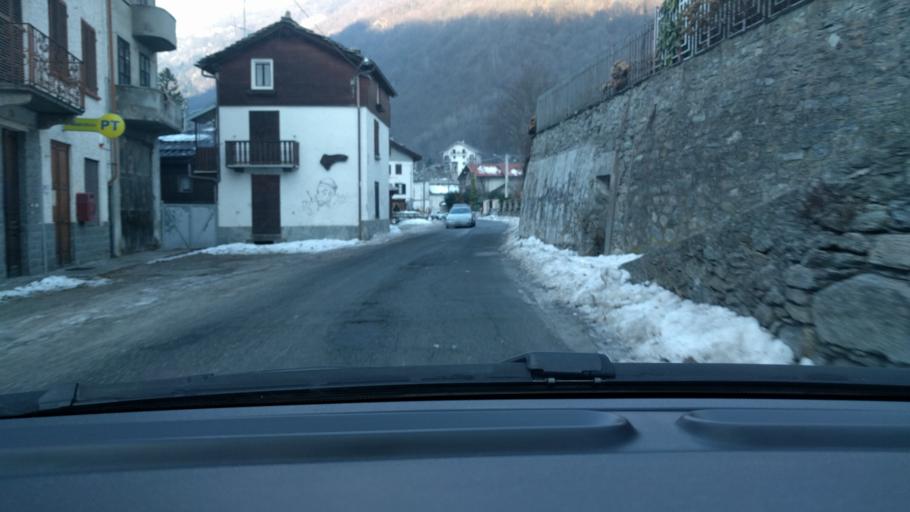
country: IT
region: Piedmont
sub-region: Provincia di Torino
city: Groscavallo
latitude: 45.3692
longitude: 7.2821
